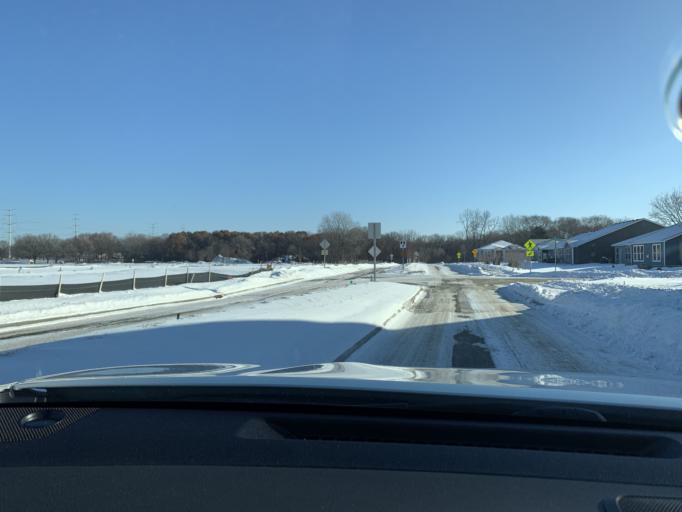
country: US
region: Minnesota
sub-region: Anoka County
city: Fridley
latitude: 45.0944
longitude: -93.2610
